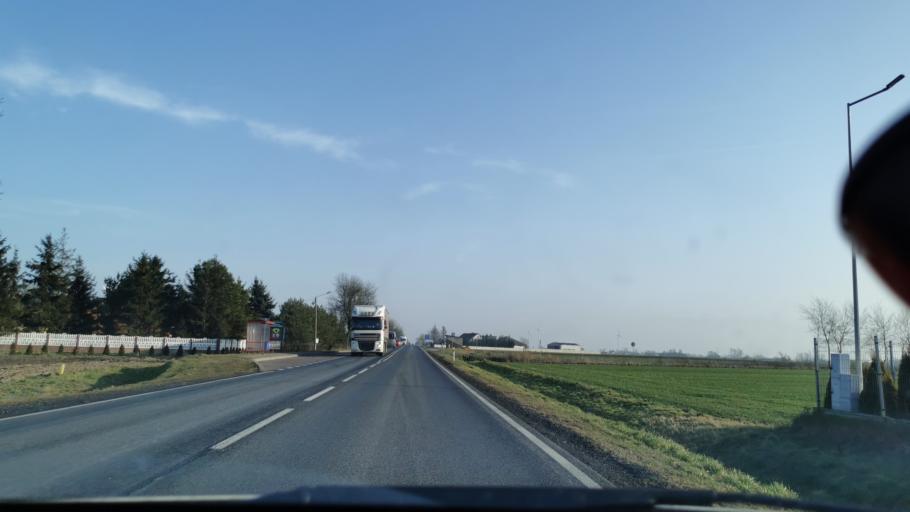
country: PL
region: Lodz Voivodeship
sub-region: Powiat sieradzki
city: Blaszki
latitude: 51.6760
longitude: 18.3569
